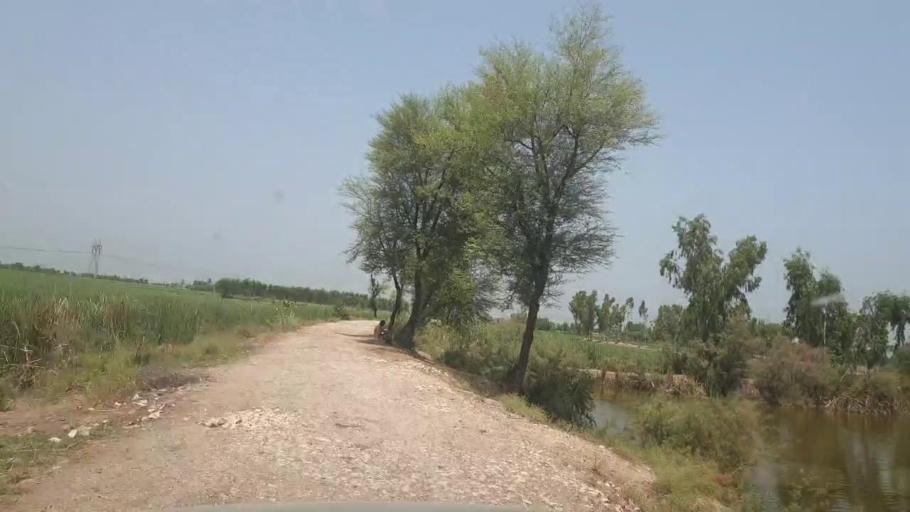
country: PK
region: Sindh
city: Lakhi
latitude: 27.8583
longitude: 68.6244
